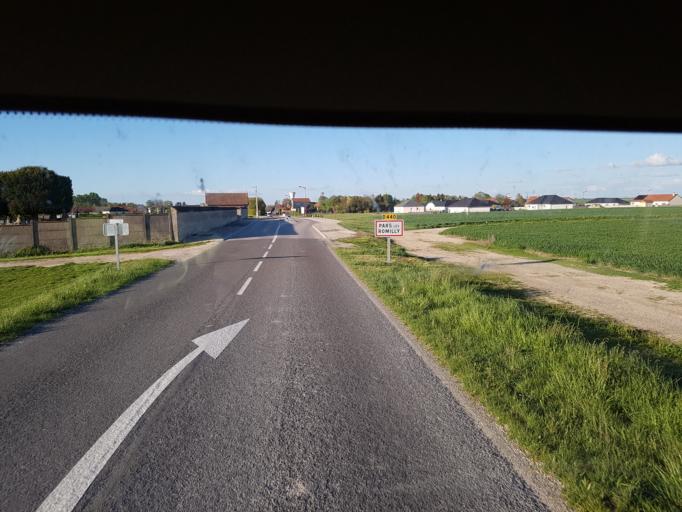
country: FR
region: Champagne-Ardenne
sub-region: Departement de l'Aube
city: Romilly-sur-Seine
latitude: 48.4791
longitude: 3.7267
